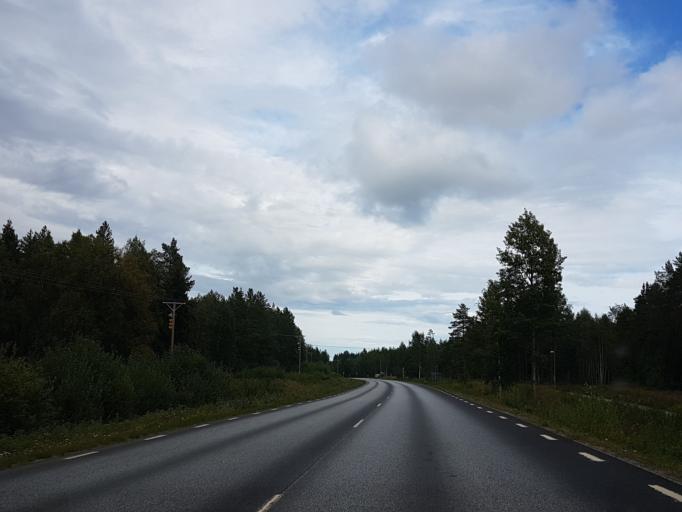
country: SE
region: Vaesterbotten
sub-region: Umea Kommun
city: Ersmark
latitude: 63.8102
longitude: 20.3829
